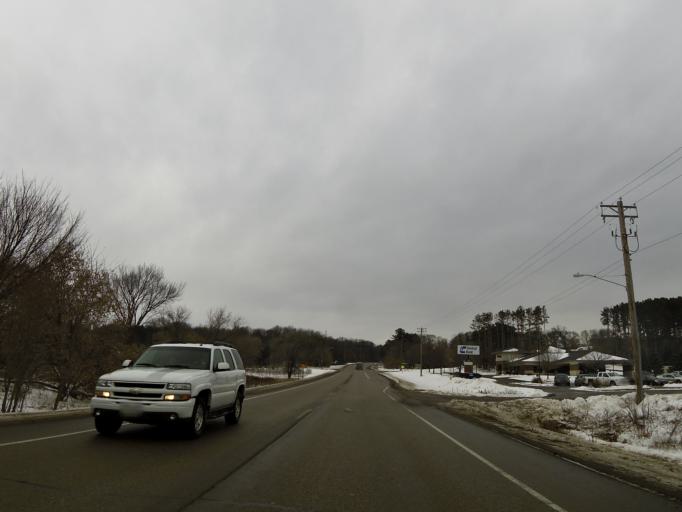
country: US
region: Wisconsin
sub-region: Saint Croix County
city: North Hudson
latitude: 45.0041
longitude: -92.7538
